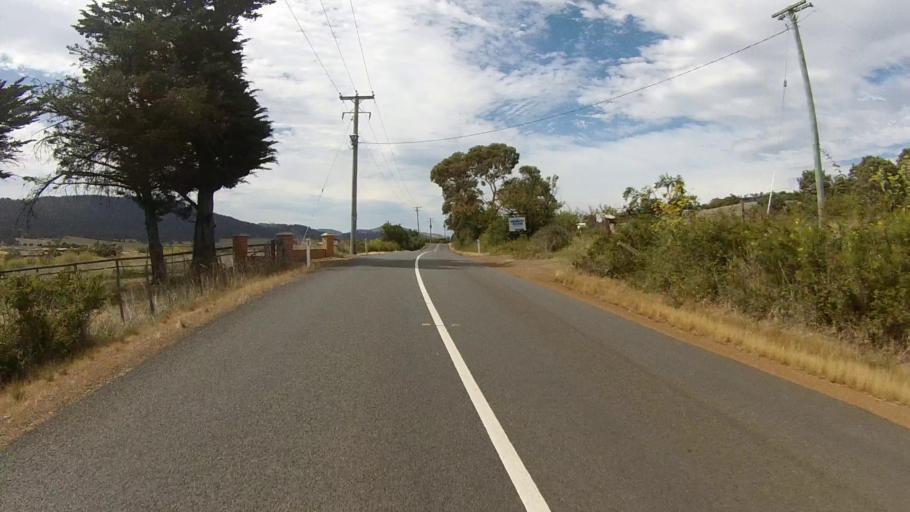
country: AU
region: Tasmania
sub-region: Brighton
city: Old Beach
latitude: -42.7041
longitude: 147.3656
